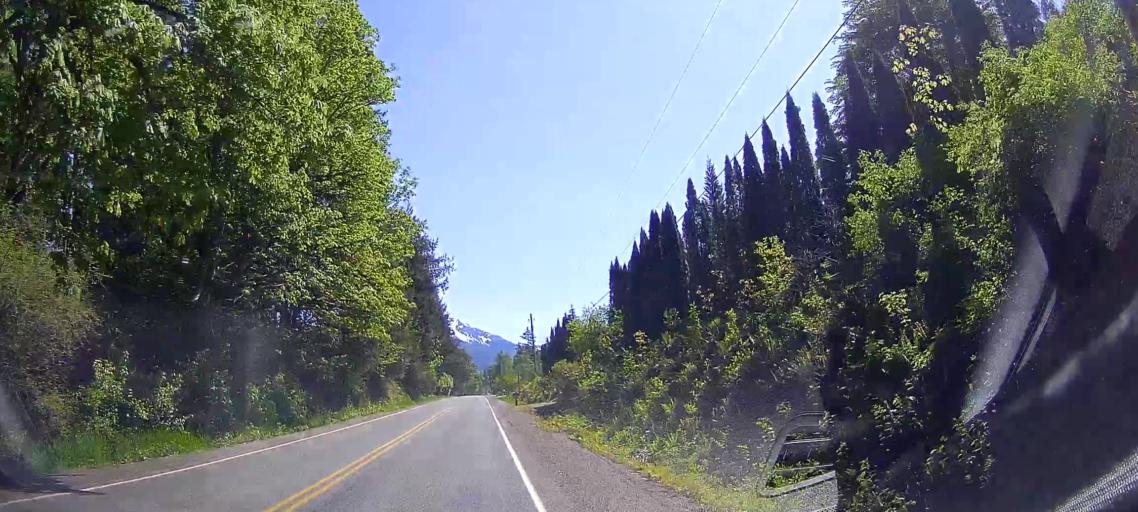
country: US
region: Washington
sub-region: Snohomish County
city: Darrington
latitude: 48.5183
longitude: -121.7568
